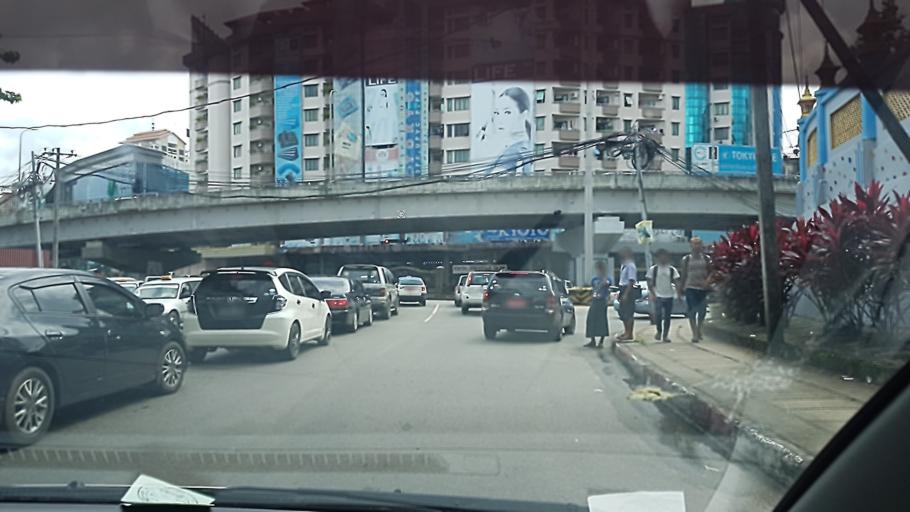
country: MM
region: Yangon
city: Yangon
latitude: 16.8075
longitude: 96.1540
